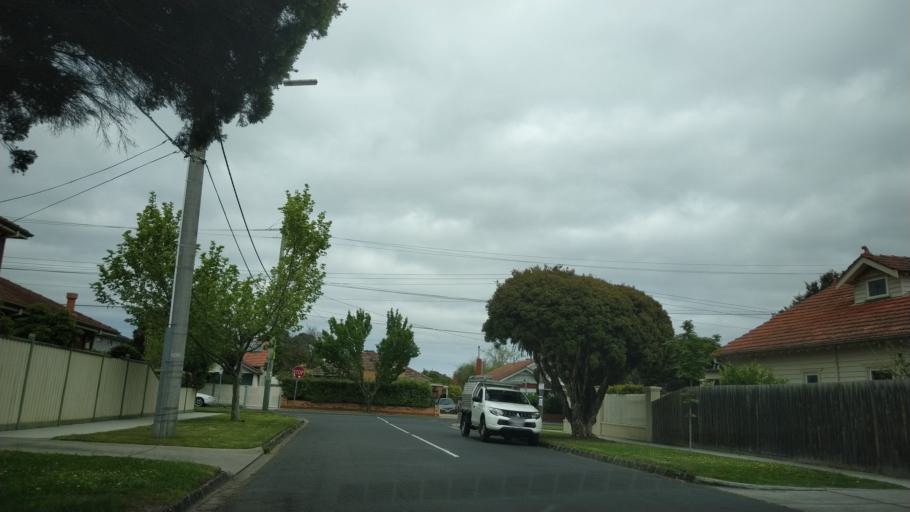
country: AU
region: Victoria
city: Murrumbeena
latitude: -37.8972
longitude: 145.0692
